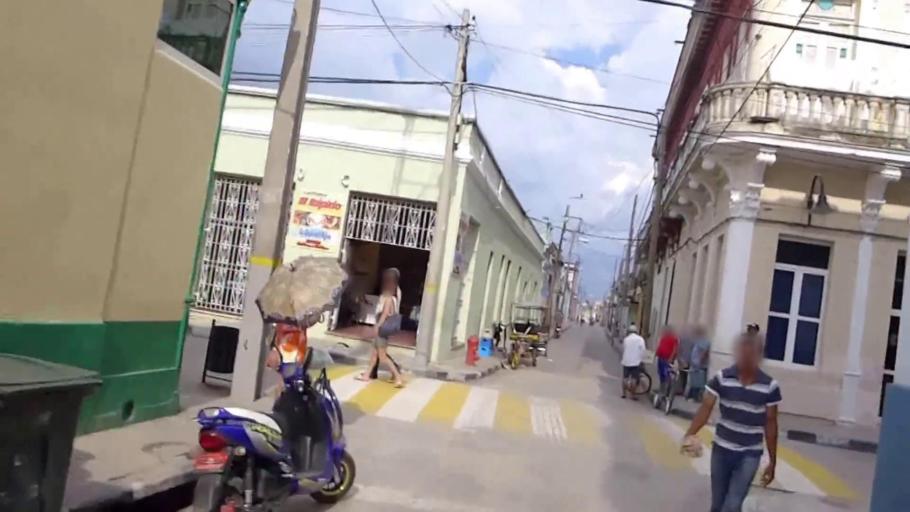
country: CU
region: Camaguey
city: Camaguey
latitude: 21.3866
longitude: -77.9167
